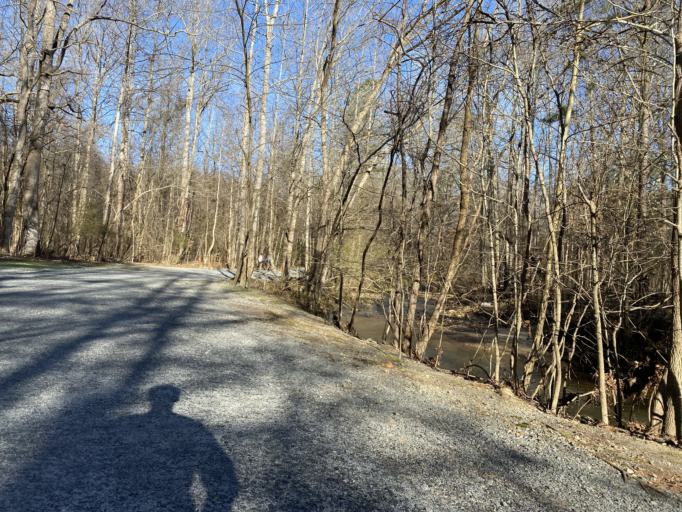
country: US
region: Georgia
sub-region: Cobb County
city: Kennesaw
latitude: 34.0532
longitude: -84.6329
